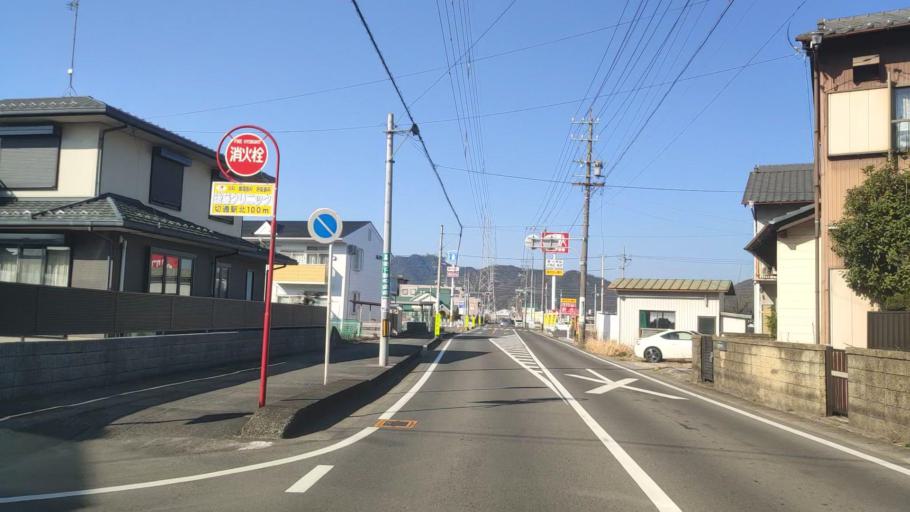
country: JP
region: Gifu
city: Gifu-shi
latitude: 35.4015
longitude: 136.7909
